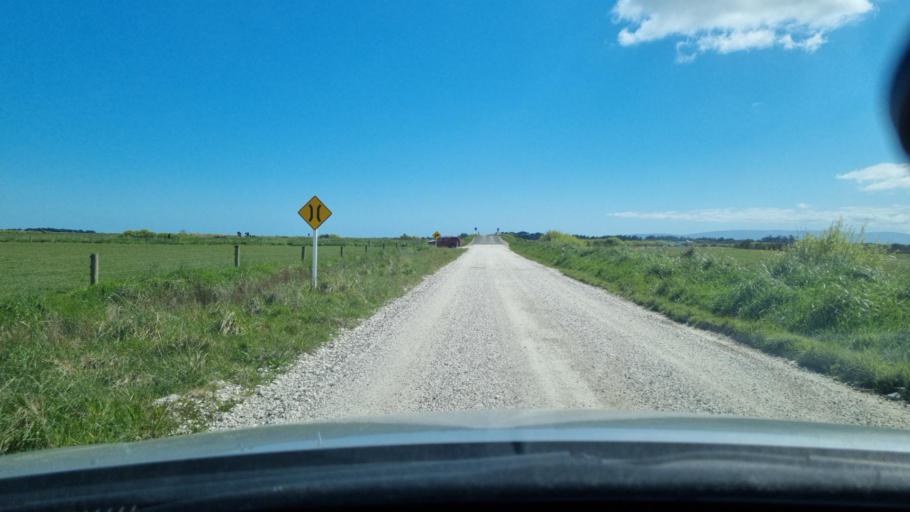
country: NZ
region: Southland
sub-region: Invercargill City
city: Invercargill
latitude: -46.3693
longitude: 168.2531
